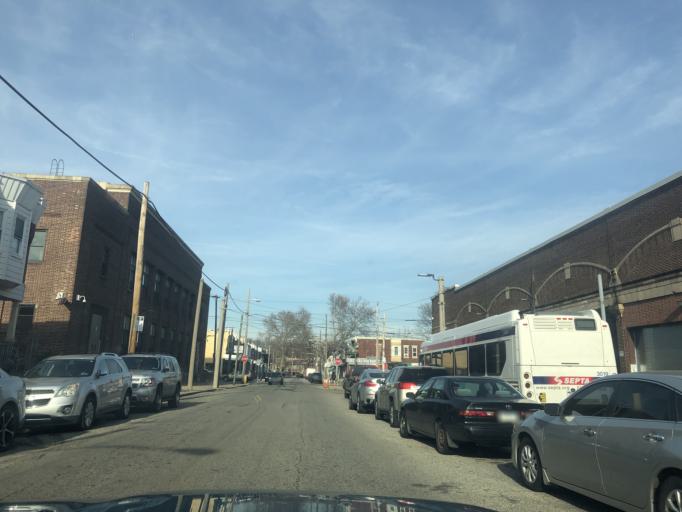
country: US
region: Pennsylvania
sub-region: Delaware County
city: Millbourne
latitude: 39.9671
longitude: -75.2377
